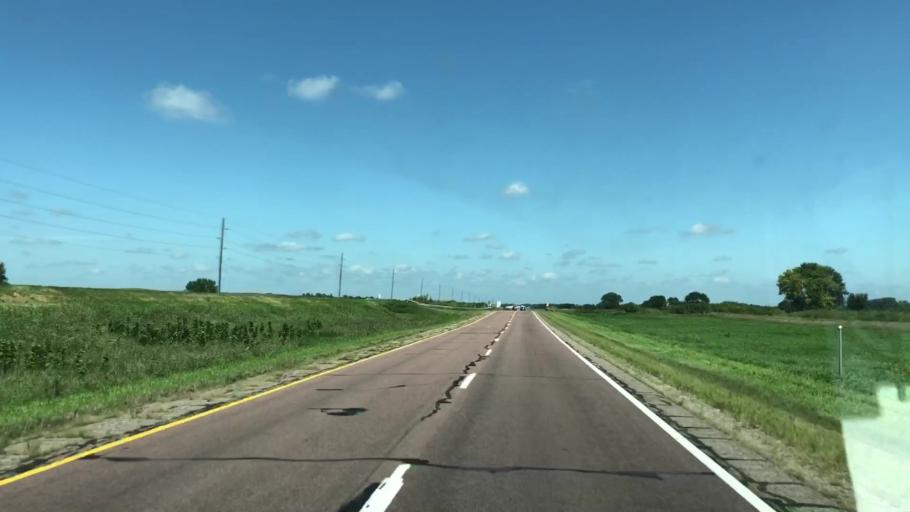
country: US
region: Iowa
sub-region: Plymouth County
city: Le Mars
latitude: 42.6830
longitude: -96.2671
